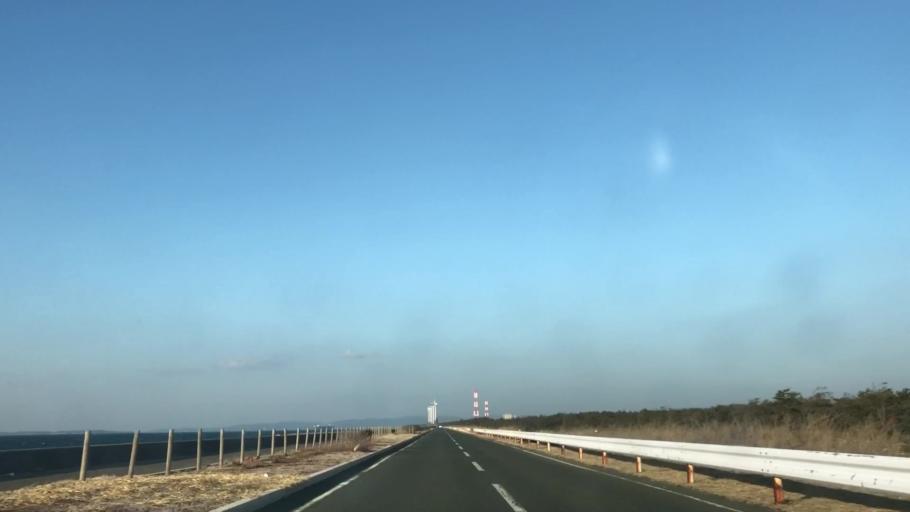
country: JP
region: Aichi
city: Toyohama
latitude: 34.6170
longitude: 137.0405
